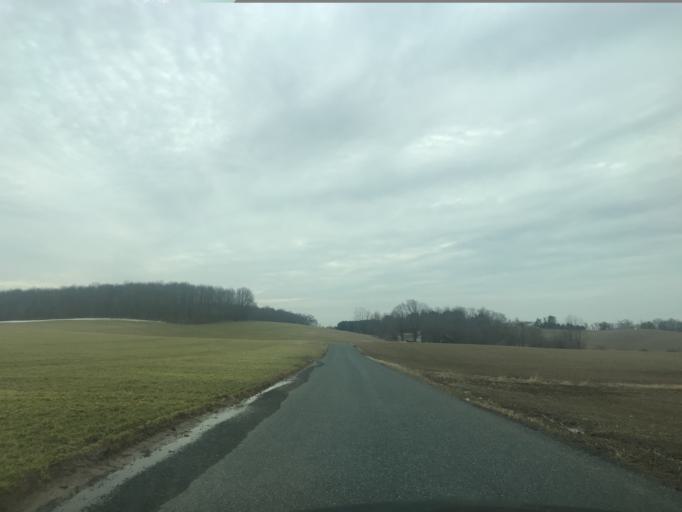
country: US
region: Maryland
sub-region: Harford County
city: Jarrettsville
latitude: 39.6773
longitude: -76.4190
